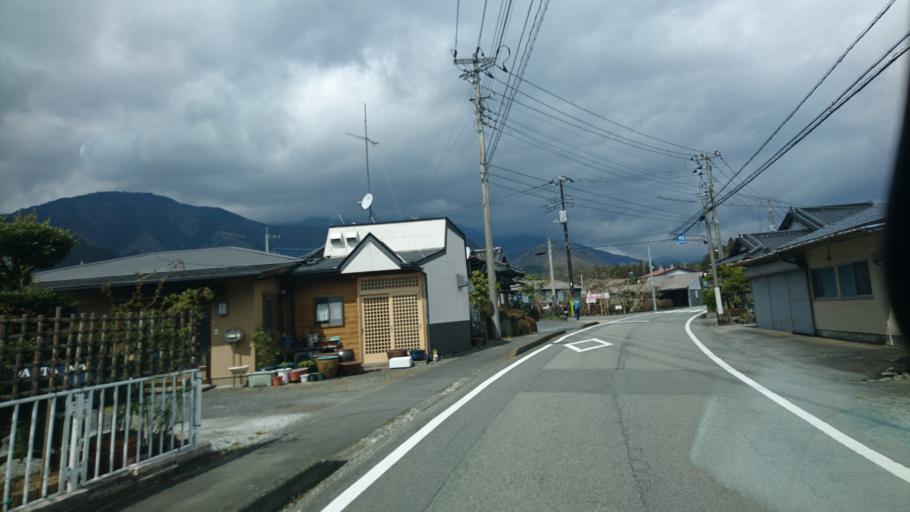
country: JP
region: Shizuoka
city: Fujinomiya
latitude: 35.3622
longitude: 138.5643
